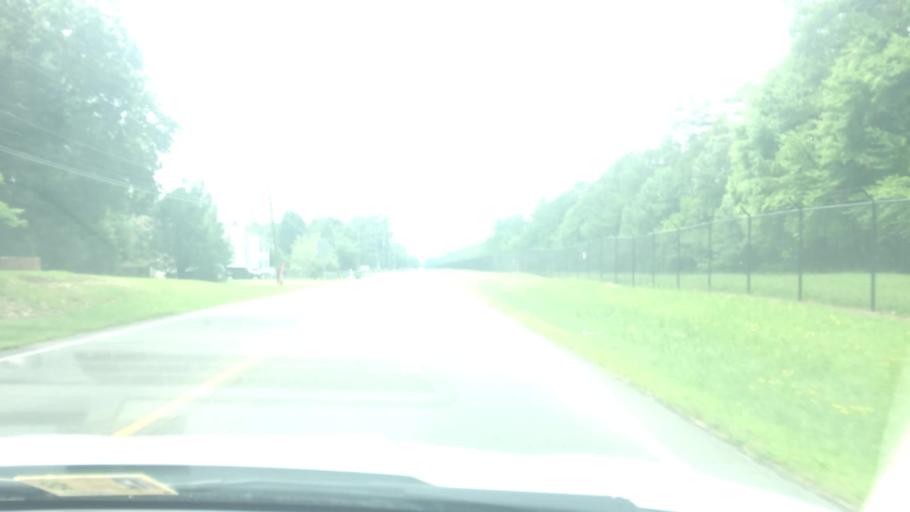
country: US
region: Virginia
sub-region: York County
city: Yorktown
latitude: 37.2289
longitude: -76.5587
